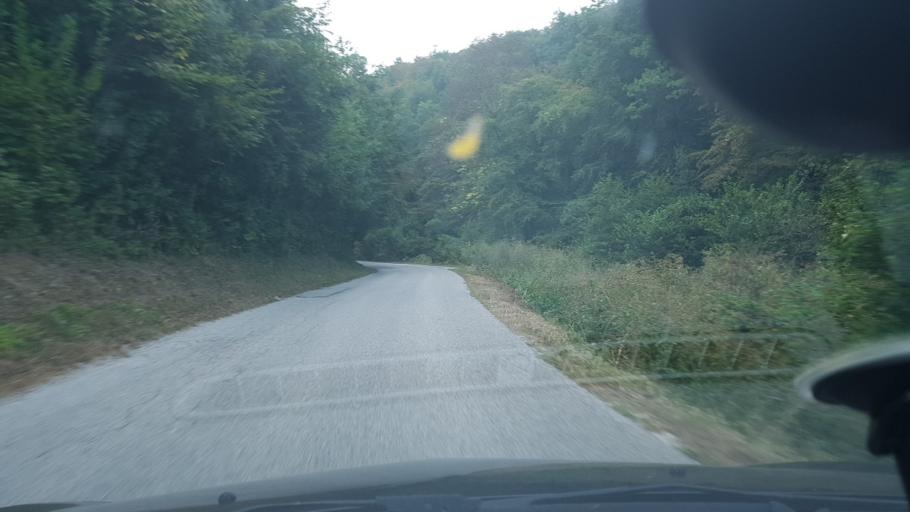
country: SI
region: Krsko
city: Senovo
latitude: 46.0205
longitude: 15.5048
